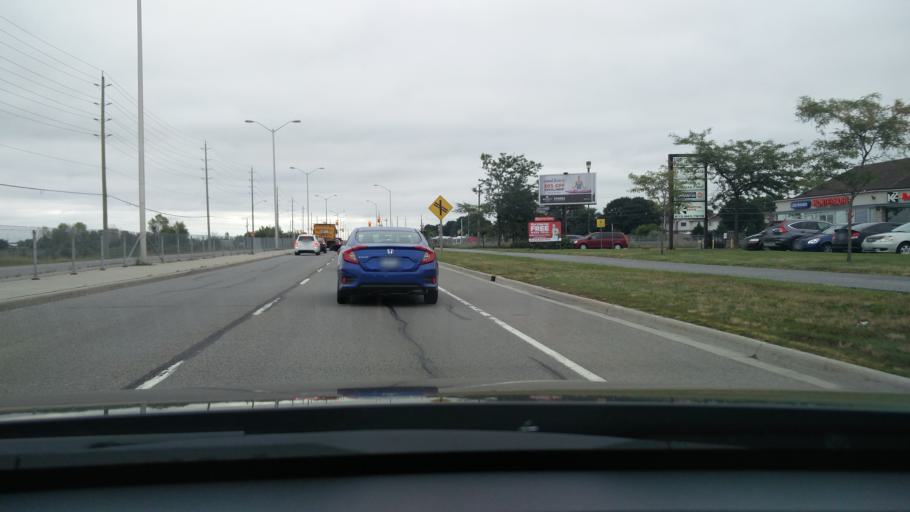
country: CA
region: Ontario
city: Bells Corners
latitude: 45.2942
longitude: -75.7422
